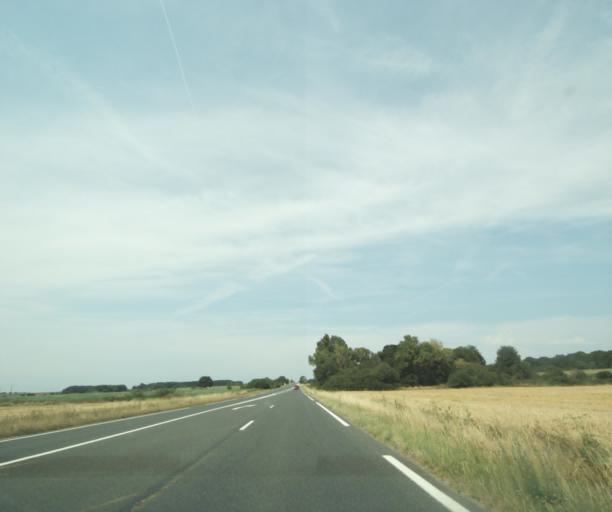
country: FR
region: Centre
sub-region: Departement d'Indre-et-Loire
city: Sorigny
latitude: 47.1842
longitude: 0.6615
